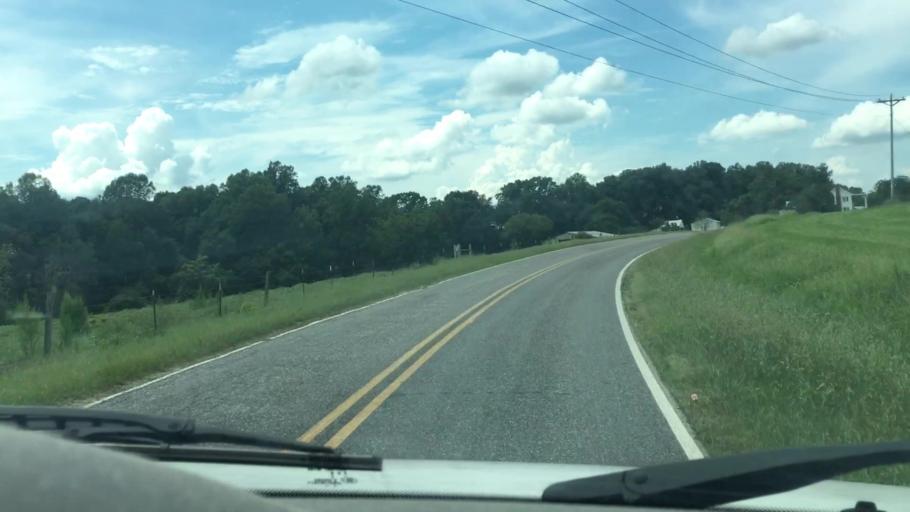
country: US
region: North Carolina
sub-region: Iredell County
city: Mooresville
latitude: 35.6625
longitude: -80.8139
